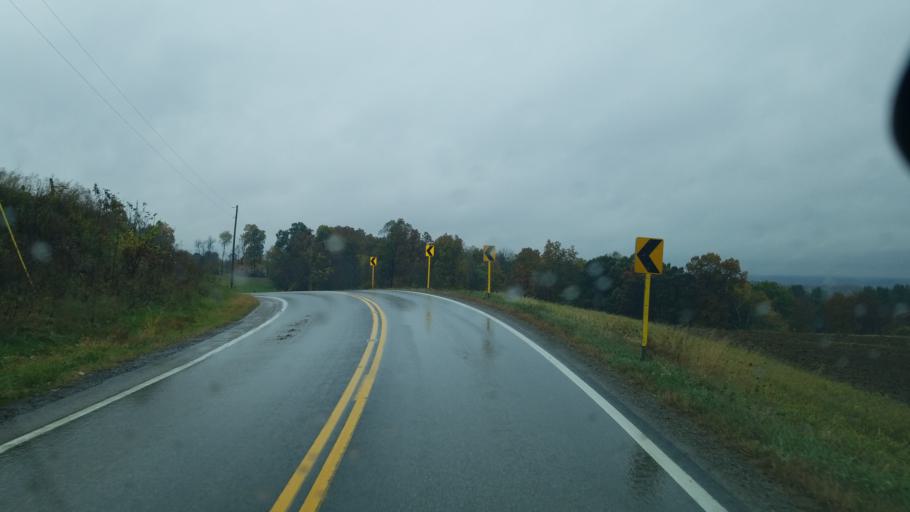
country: US
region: Ohio
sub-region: Coshocton County
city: Coshocton
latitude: 40.4142
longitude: -81.8099
